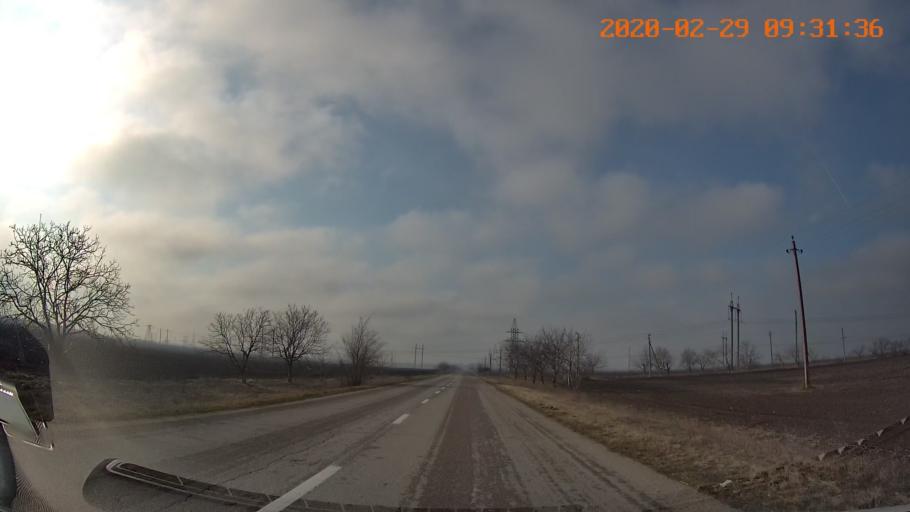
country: MD
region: Telenesti
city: Dnestrovsc
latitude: 46.6506
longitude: 29.9104
